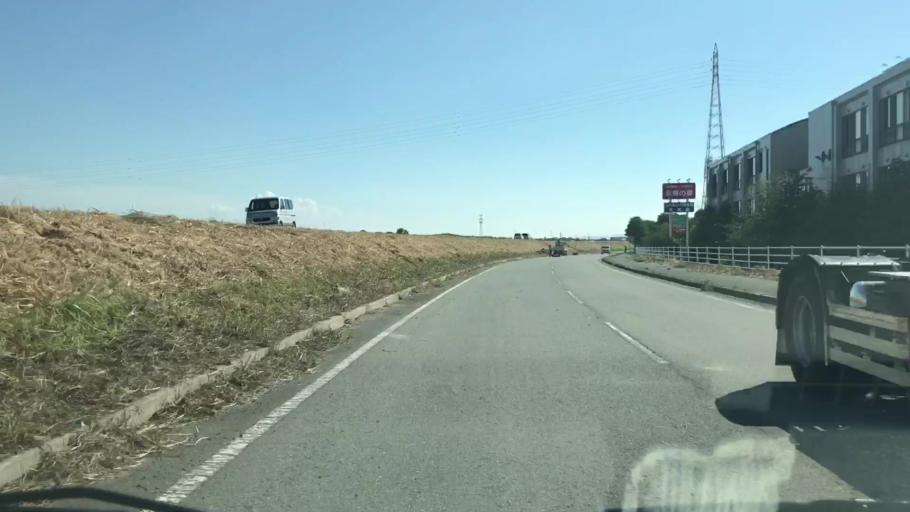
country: JP
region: Saga Prefecture
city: Okawa
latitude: 33.2323
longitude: 130.3781
